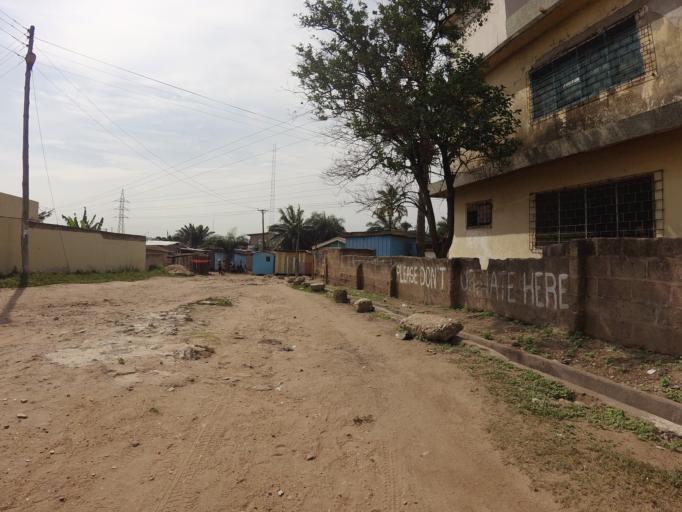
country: GH
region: Greater Accra
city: Dome
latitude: 5.6231
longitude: -0.2313
